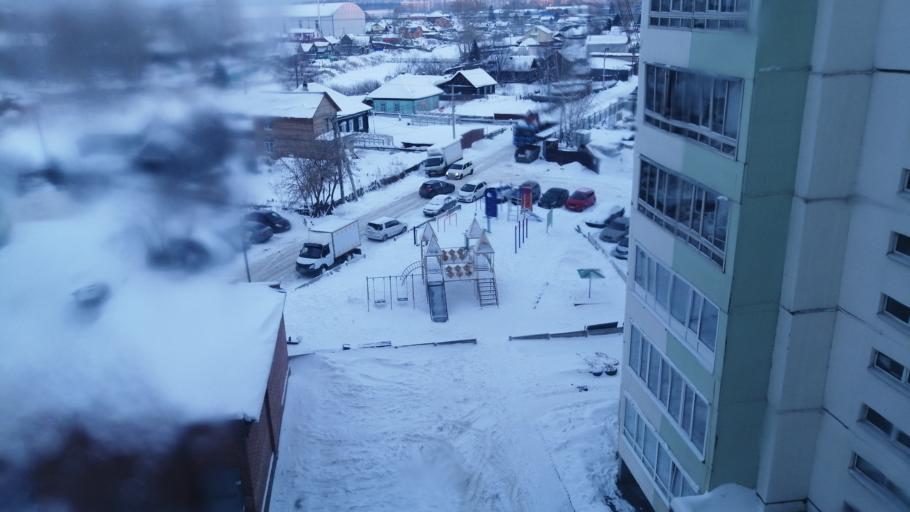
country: RU
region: Tomsk
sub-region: Tomskiy Rayon
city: Tomsk
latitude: 56.5226
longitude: 84.9375
